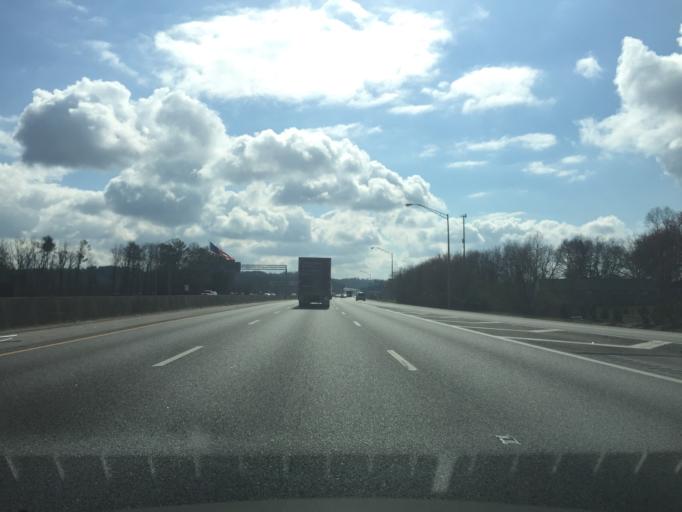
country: US
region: Georgia
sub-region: Catoosa County
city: Indian Springs
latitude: 34.9883
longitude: -85.2029
